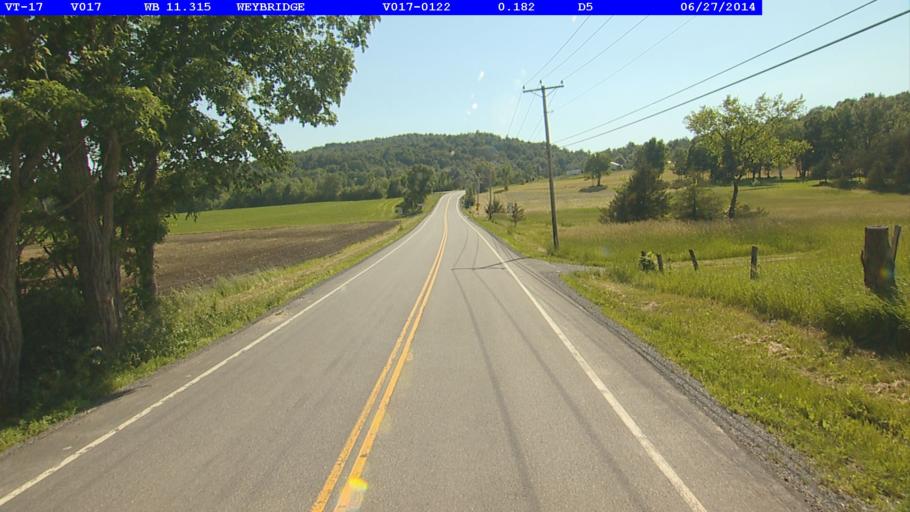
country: US
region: Vermont
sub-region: Addison County
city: Vergennes
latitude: 44.0857
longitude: -73.2472
